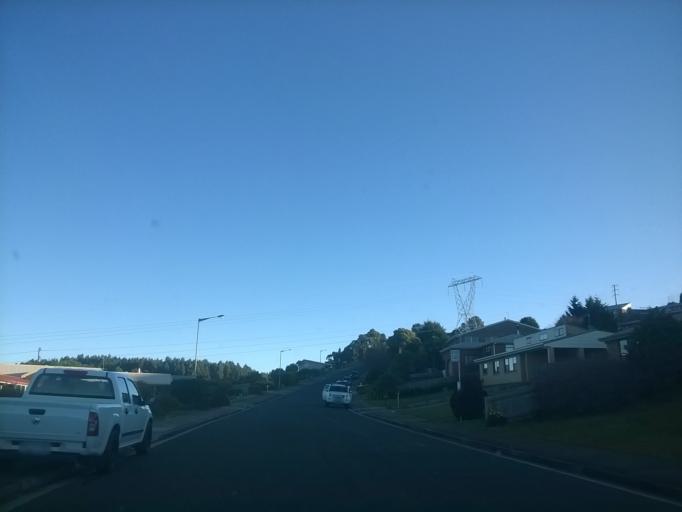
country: AU
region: Tasmania
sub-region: Burnie
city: Burnie
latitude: -41.0823
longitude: 145.9038
